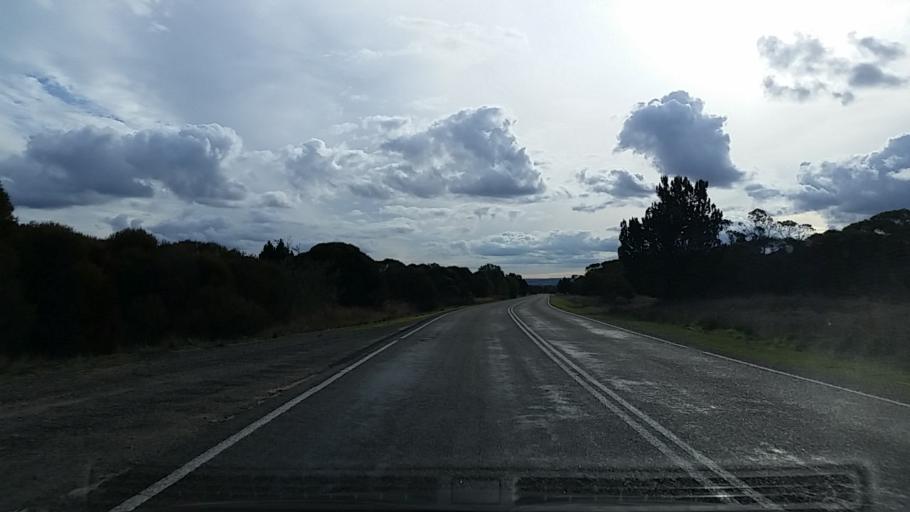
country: AU
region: South Australia
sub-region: Murray Bridge
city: Murray Bridge
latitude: -35.1332
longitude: 139.1971
